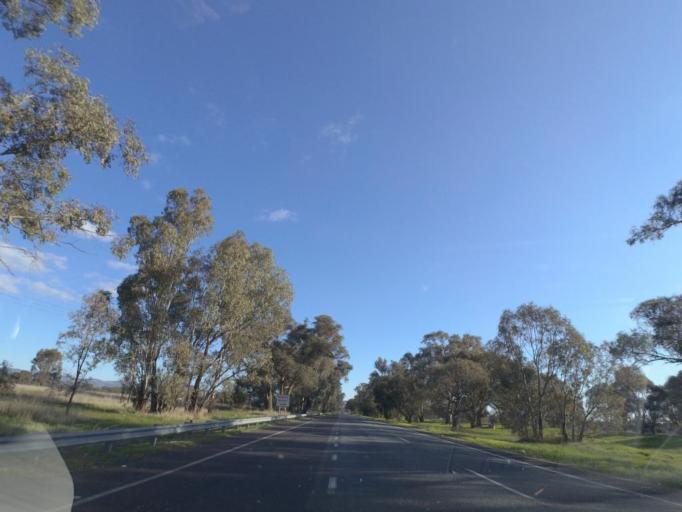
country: AU
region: Victoria
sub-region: Benalla
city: Benalla
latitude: -36.6973
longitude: 145.6564
